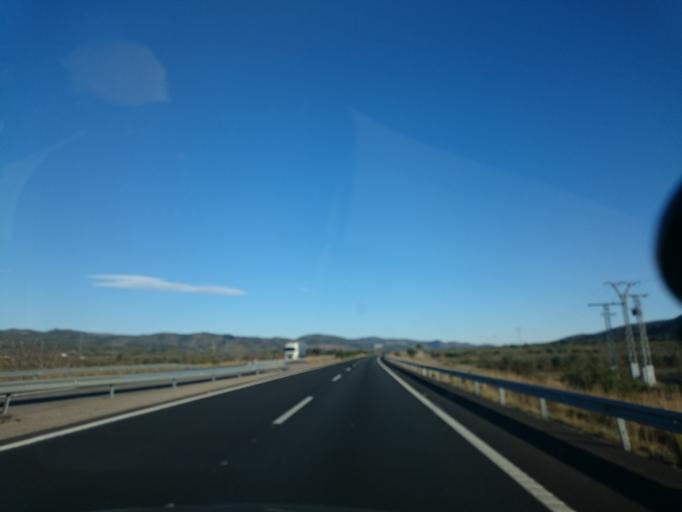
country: ES
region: Valencia
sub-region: Provincia de Castello
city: Alcala de Xivert
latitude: 40.3046
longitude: 0.2383
